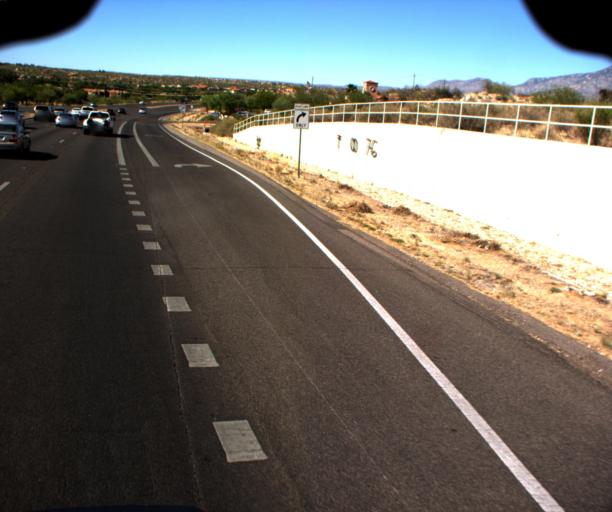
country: US
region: Arizona
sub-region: Pima County
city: Oro Valley
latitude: 32.3889
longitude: -110.9641
